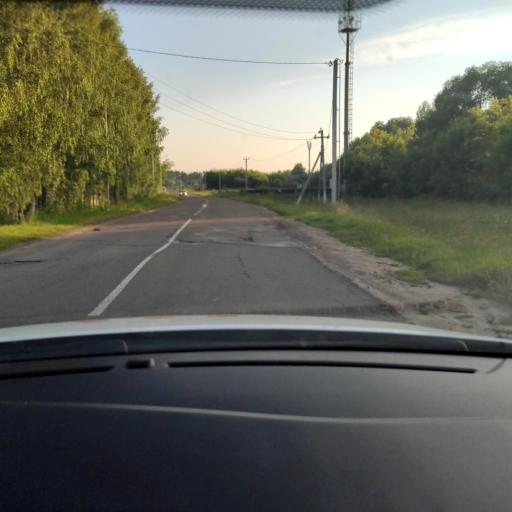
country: RU
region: Tatarstan
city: Vysokaya Gora
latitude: 55.9732
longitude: 49.3061
